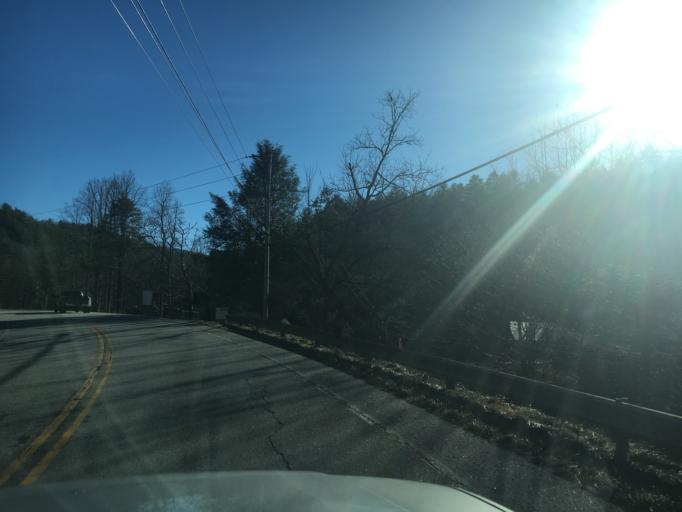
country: US
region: Georgia
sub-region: Union County
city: Blairsville
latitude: 34.7816
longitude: -83.9097
